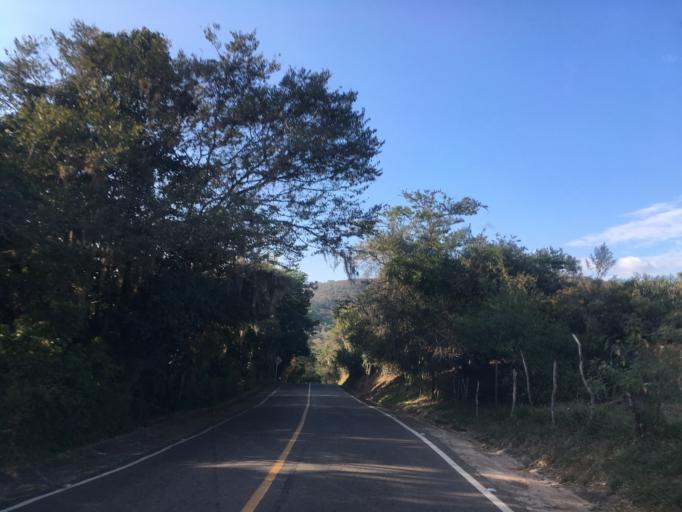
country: CO
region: Santander
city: Barichara
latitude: 6.6364
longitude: -73.2015
